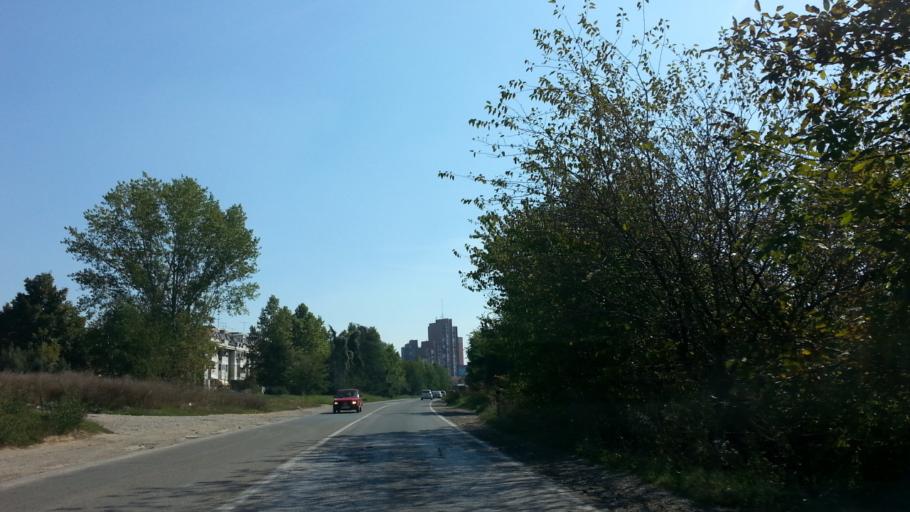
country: RS
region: Central Serbia
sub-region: Belgrade
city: Rakovica
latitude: 44.7389
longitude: 20.4163
